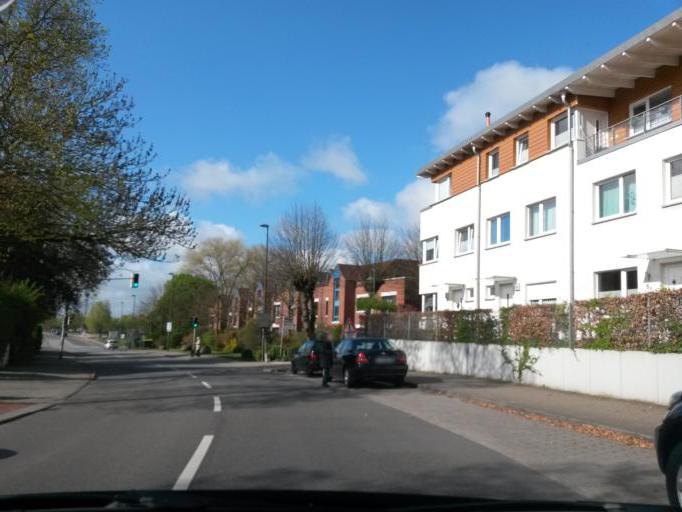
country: DE
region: Schleswig-Holstein
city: Wedel
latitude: 53.5833
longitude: 9.6967
